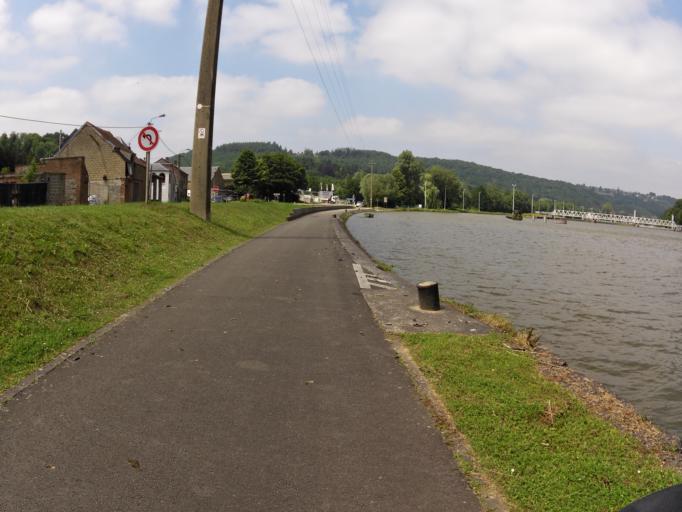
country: BE
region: Wallonia
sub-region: Province de Namur
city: Hastiere-Lavaux
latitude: 50.1972
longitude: 4.8202
